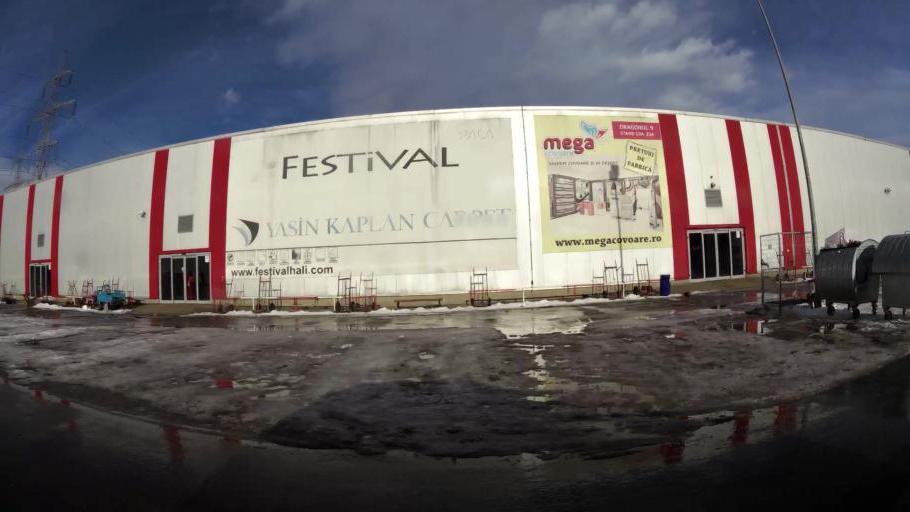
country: RO
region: Ilfov
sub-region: Voluntari City
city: Voluntari
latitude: 44.4754
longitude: 26.1823
